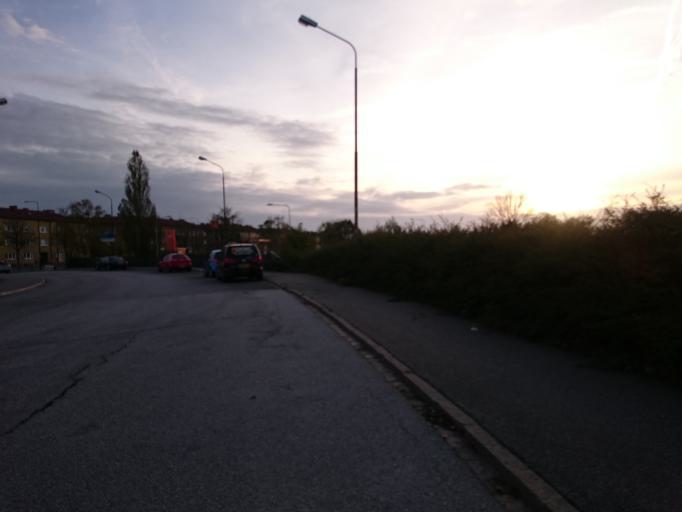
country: SE
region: Skane
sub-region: Burlovs Kommun
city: Arloev
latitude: 55.6170
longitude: 13.0458
